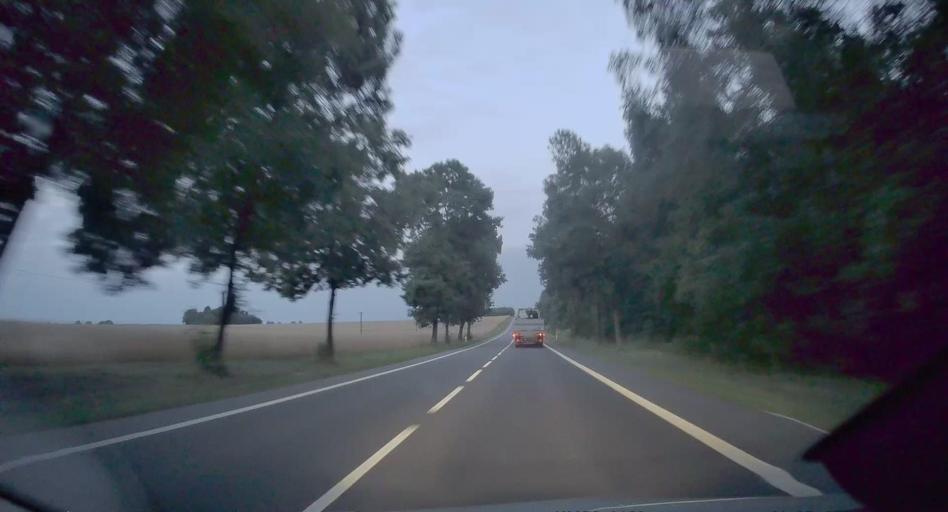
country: PL
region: Silesian Voivodeship
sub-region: Powiat klobucki
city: Opatow
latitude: 50.9423
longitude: 18.8383
